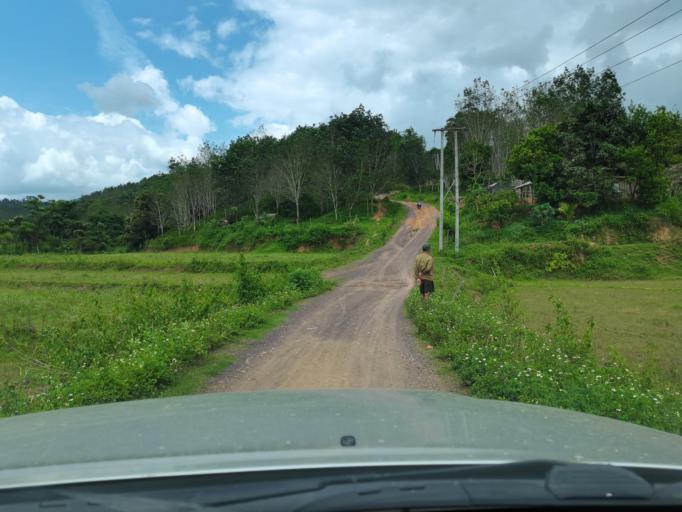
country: LA
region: Loungnamtha
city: Muang Long
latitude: 20.7008
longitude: 101.0204
